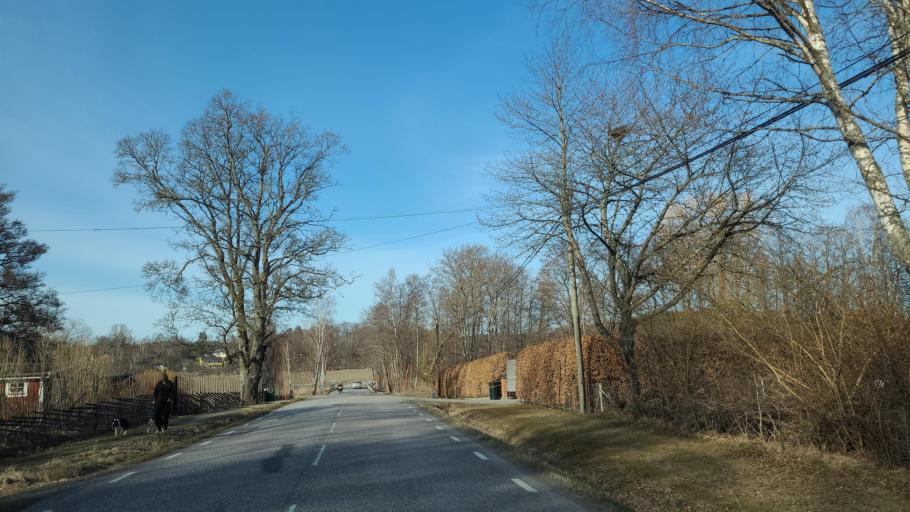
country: SE
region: Stockholm
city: Stenhamra
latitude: 59.2780
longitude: 17.7072
